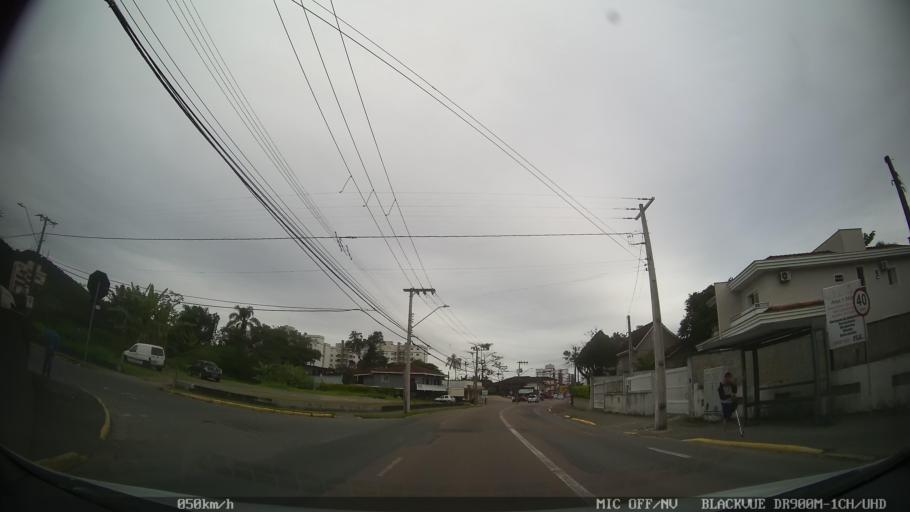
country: BR
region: Santa Catarina
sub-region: Joinville
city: Joinville
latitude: -26.2803
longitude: -48.8370
